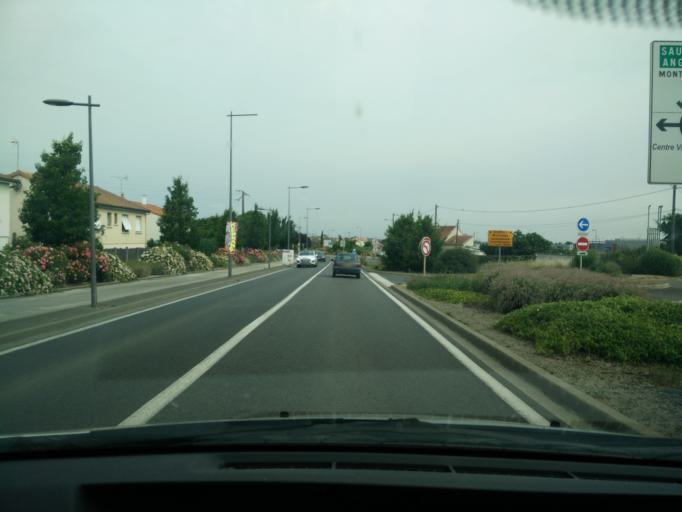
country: FR
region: Poitou-Charentes
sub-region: Departement des Deux-Sevres
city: Thouars
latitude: 46.9781
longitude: -0.1982
